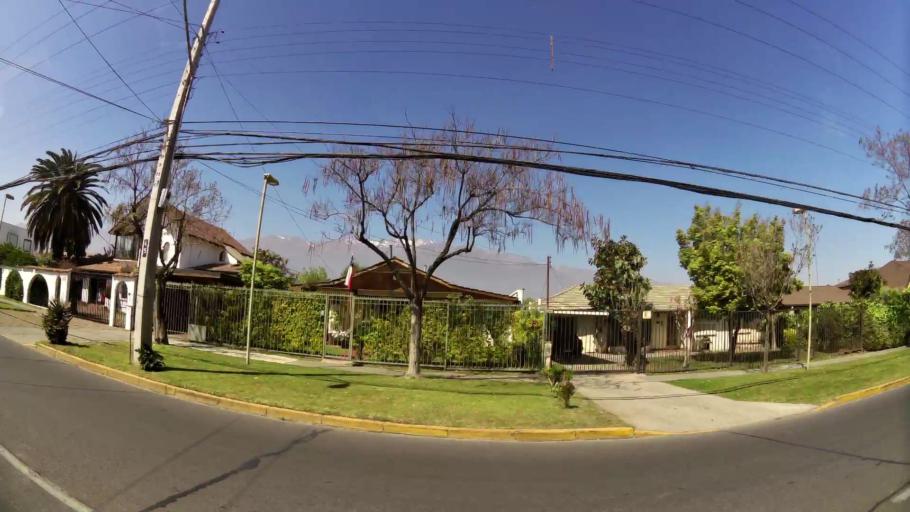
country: CL
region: Santiago Metropolitan
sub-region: Provincia de Santiago
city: Villa Presidente Frei, Nunoa, Santiago, Chile
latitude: -33.4156
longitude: -70.5505
